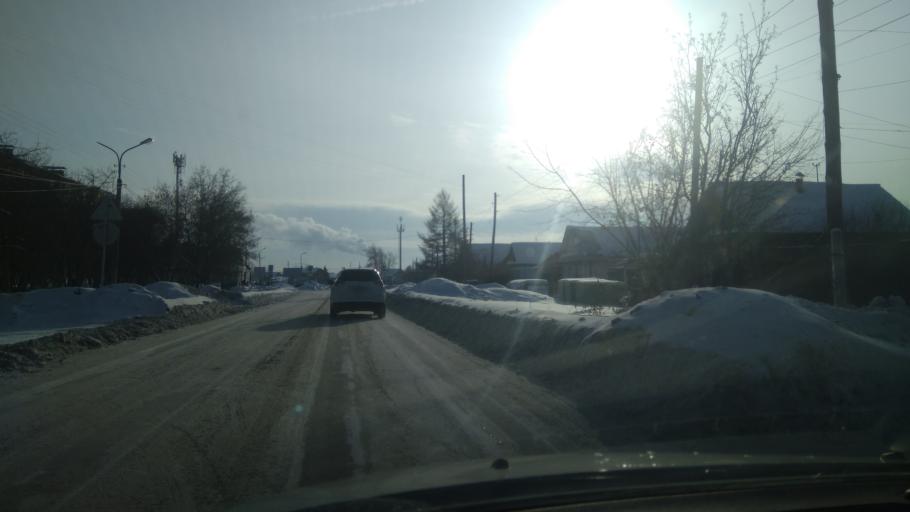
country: RU
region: Sverdlovsk
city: Sukhoy Log
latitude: 56.8941
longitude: 62.0330
